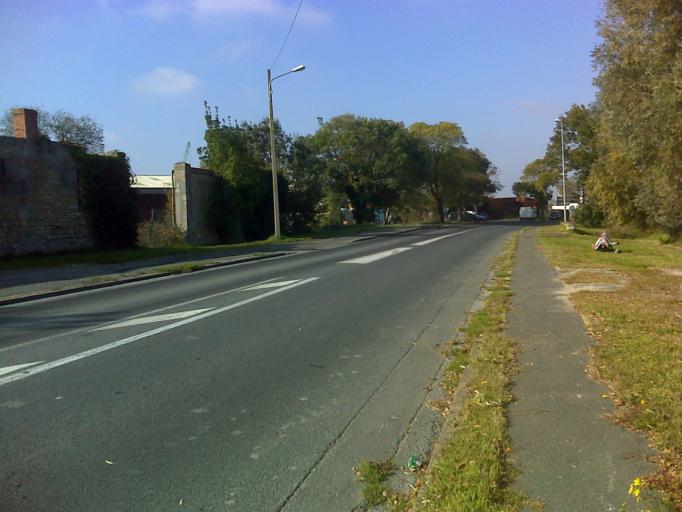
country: FR
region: Poitou-Charentes
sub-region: Departement de la Charente-Maritime
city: Breuil-Magne
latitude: 45.9504
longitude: -0.9494
